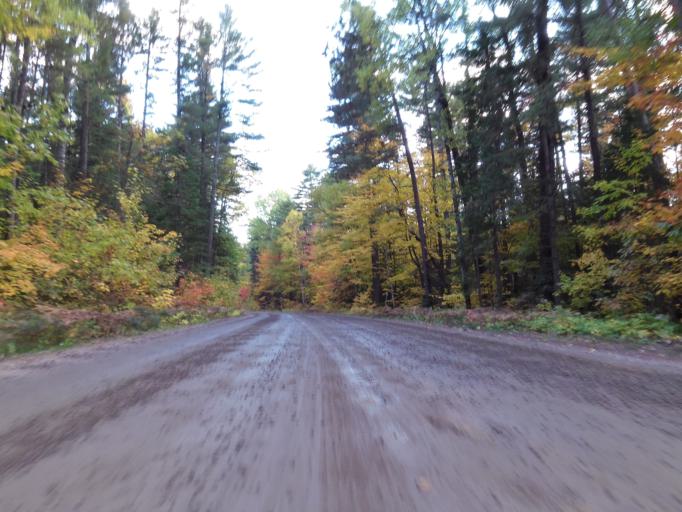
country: CA
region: Ontario
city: Deep River
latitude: 45.8983
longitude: -77.6111
